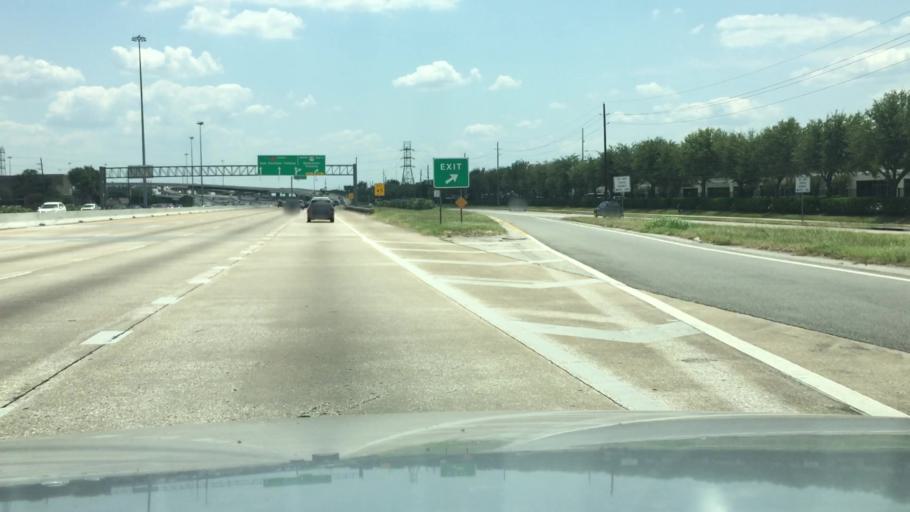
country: US
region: Texas
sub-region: Fort Bend County
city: Meadows Place
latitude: 29.6711
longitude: -95.5605
